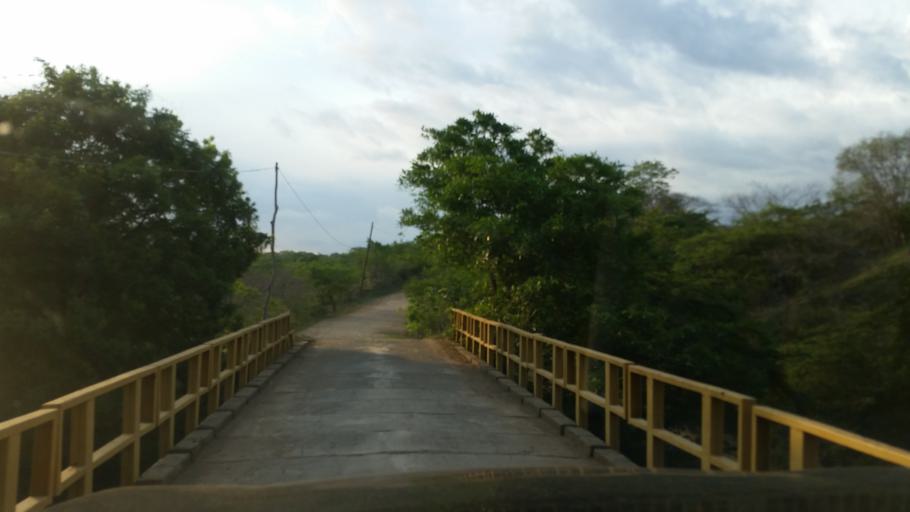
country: NI
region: Managua
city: Masachapa
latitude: 11.8060
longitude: -86.4821
